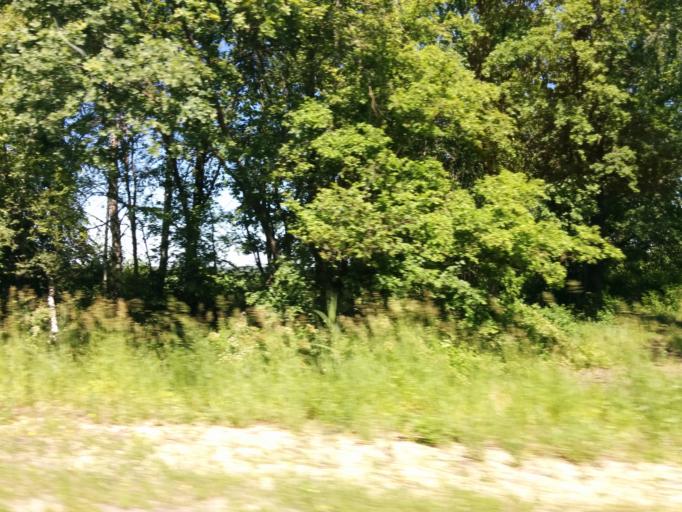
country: RU
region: Tambov
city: Morshansk
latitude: 53.5696
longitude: 41.7571
